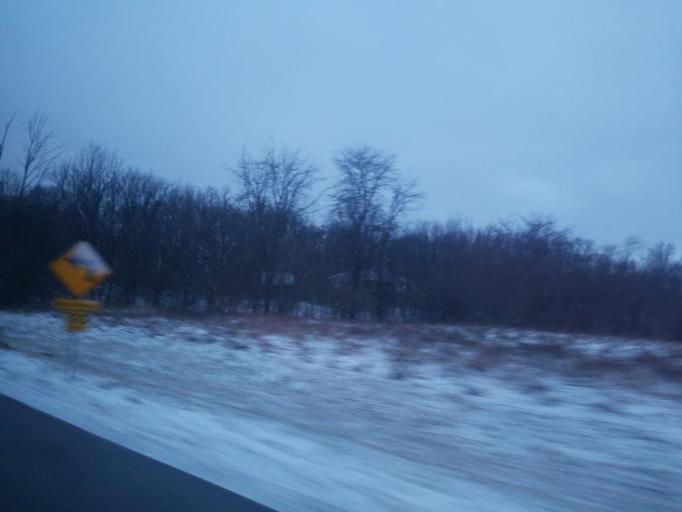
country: US
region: Ohio
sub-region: Delaware County
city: Sunbury
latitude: 40.2065
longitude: -82.8536
